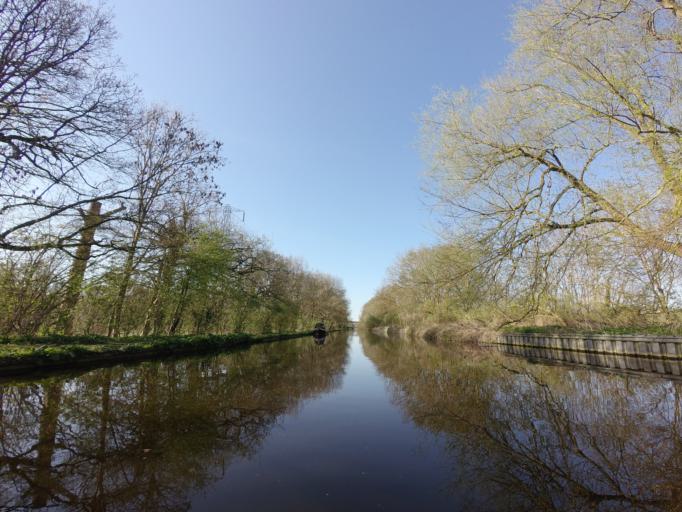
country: GB
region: England
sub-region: Buckinghamshire
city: Denham
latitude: 51.5728
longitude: -0.4820
